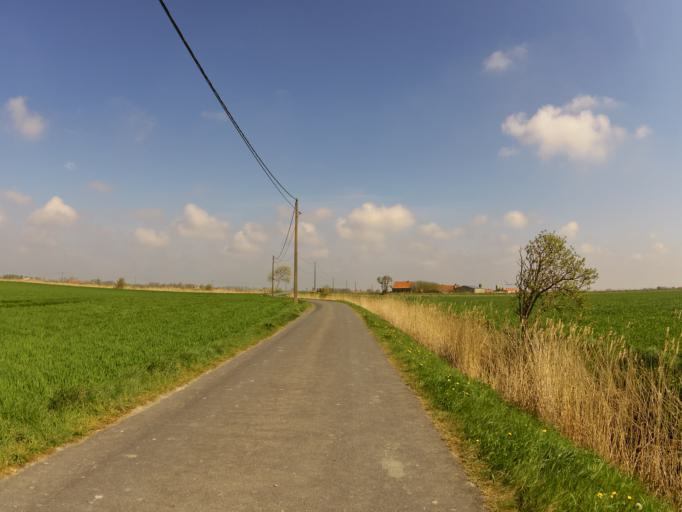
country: BE
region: Flanders
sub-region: Provincie West-Vlaanderen
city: Nieuwpoort
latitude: 51.1004
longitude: 2.7738
